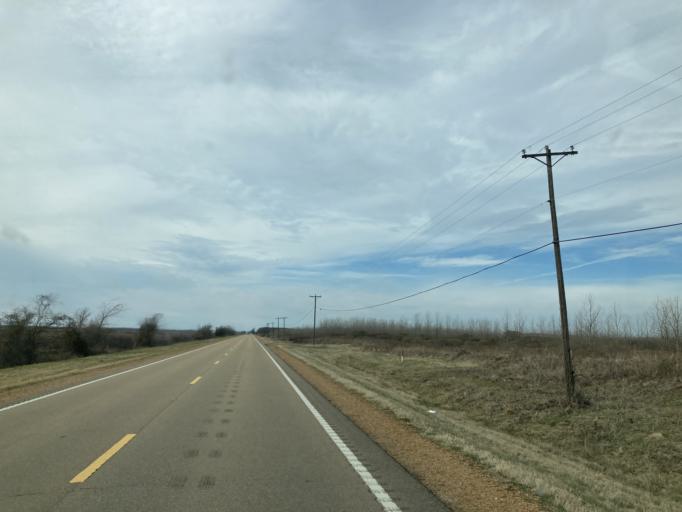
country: US
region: Mississippi
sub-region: Humphreys County
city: Belzoni
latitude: 33.1832
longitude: -90.6093
